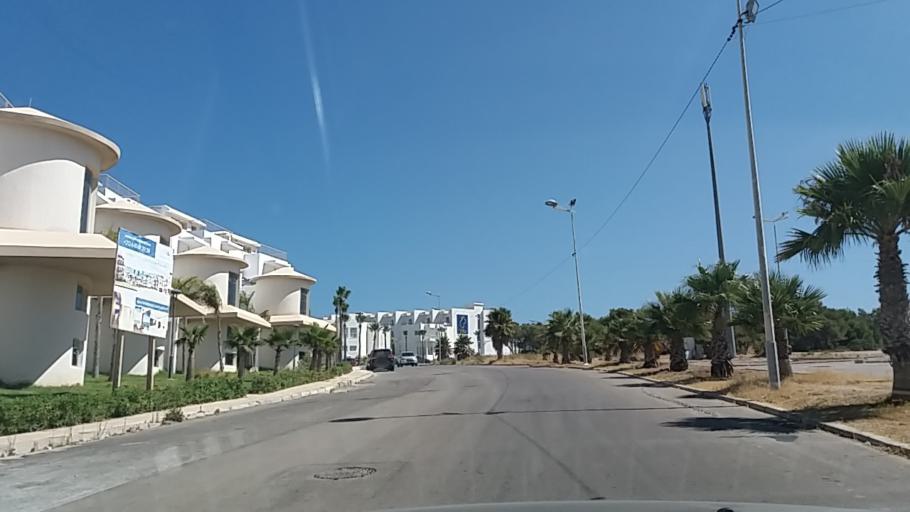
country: MA
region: Tanger-Tetouan
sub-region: Tanger-Assilah
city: Tangier
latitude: 35.7906
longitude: -5.7553
